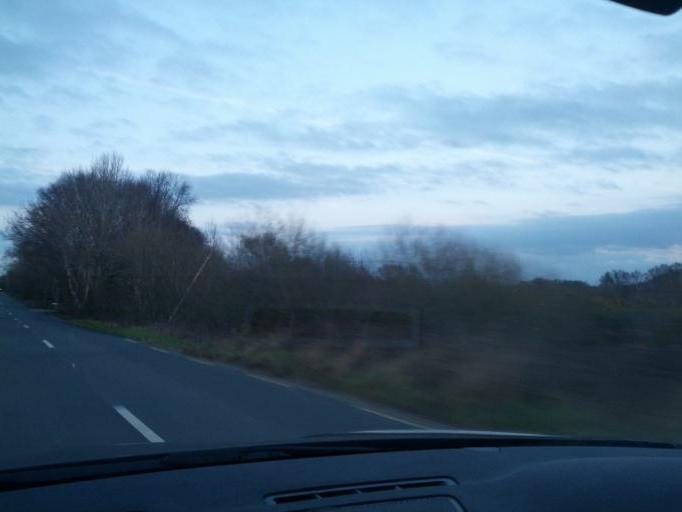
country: IE
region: Connaught
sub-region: County Galway
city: Portumna
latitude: 53.0562
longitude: -8.0982
